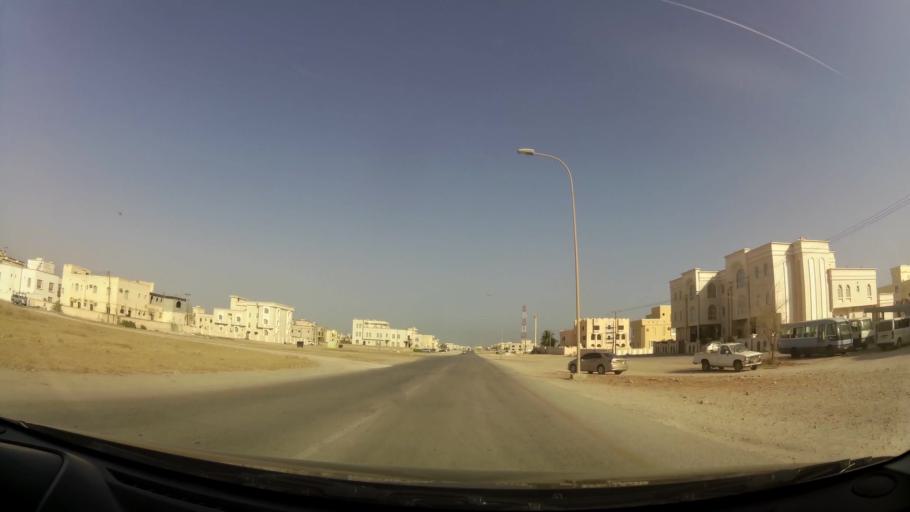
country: OM
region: Zufar
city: Salalah
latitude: 17.0205
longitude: 54.0180
